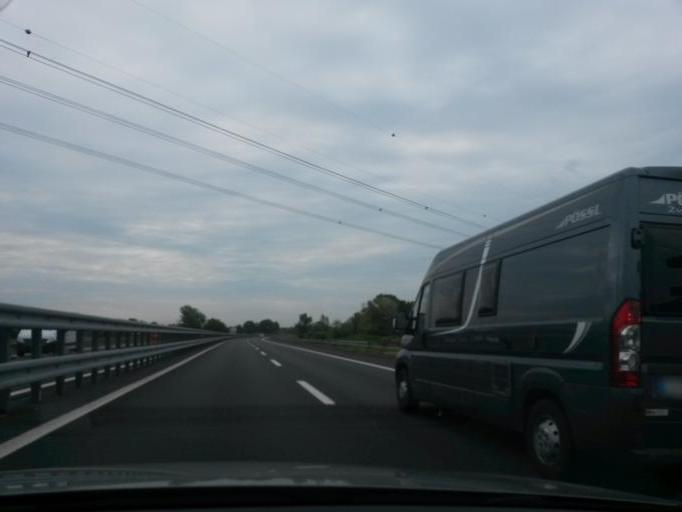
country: IT
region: Liguria
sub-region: Provincia di La Spezia
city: Arcola
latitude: 44.1263
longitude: 9.9310
